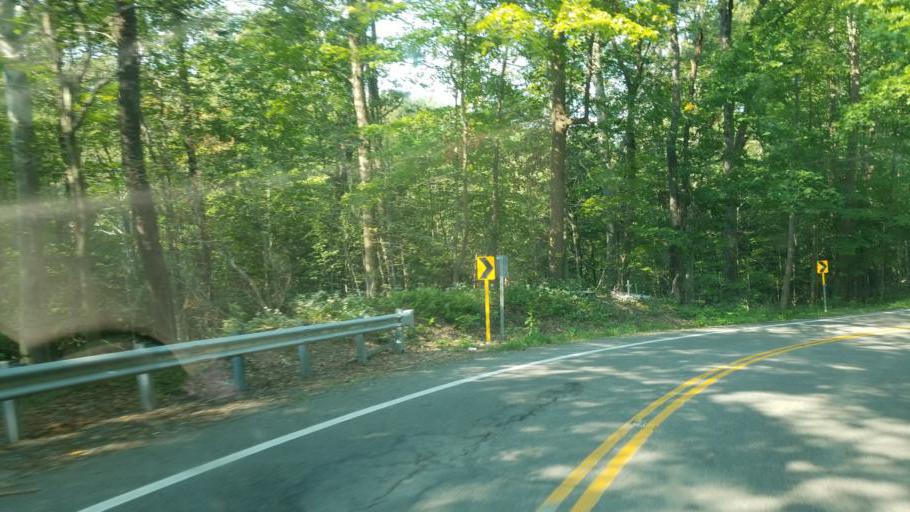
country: US
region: Ohio
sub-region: Geauga County
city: Chardon
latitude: 41.6467
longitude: -81.1852
